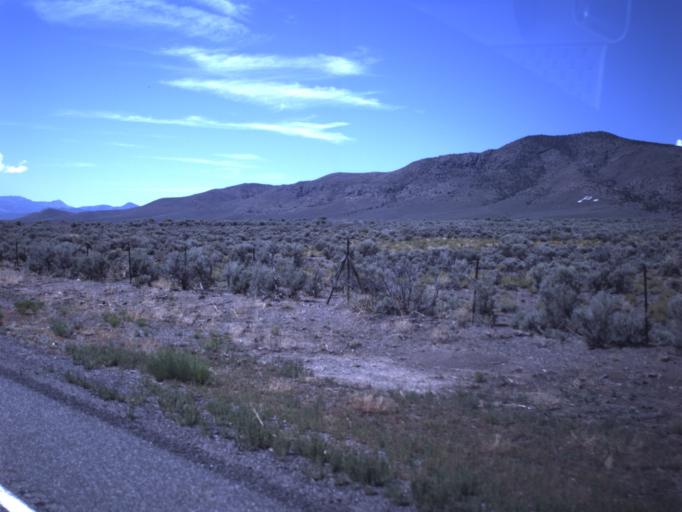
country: US
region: Utah
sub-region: Piute County
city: Junction
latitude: 38.2616
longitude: -112.2211
